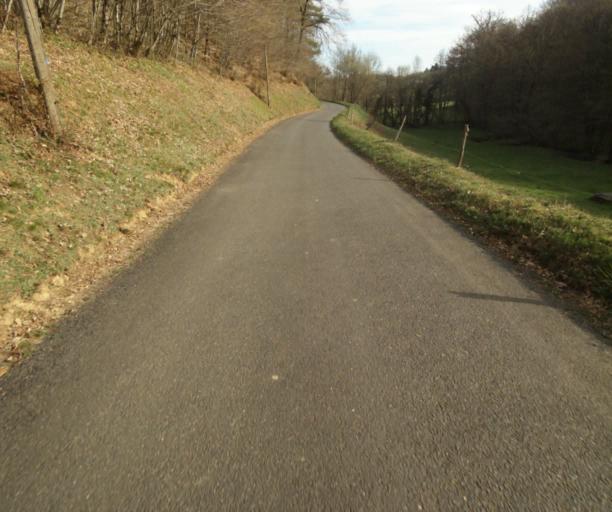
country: FR
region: Limousin
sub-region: Departement de la Correze
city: Naves
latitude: 45.2961
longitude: 1.7561
